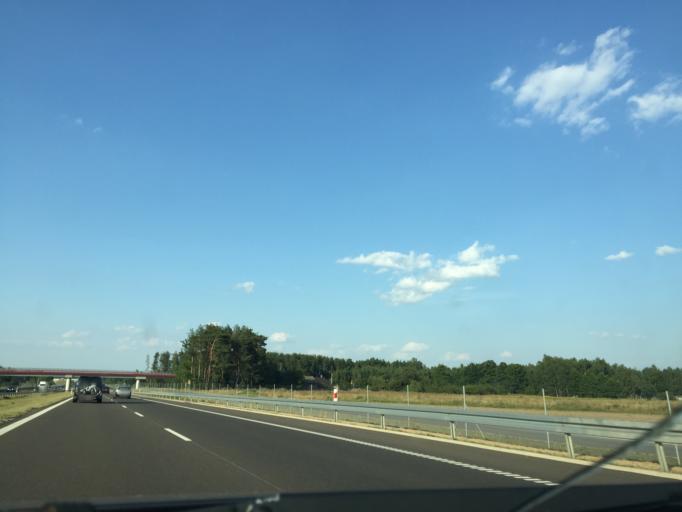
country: PL
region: Masovian Voivodeship
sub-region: Powiat radomski
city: Jedlinsk
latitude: 51.4862
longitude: 21.0675
